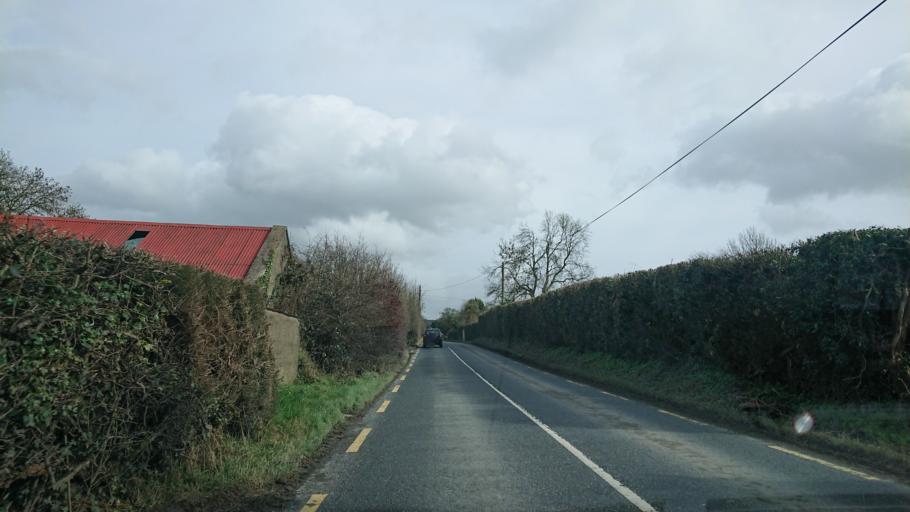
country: IE
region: Leinster
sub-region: Kildare
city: Eadestown
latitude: 53.1959
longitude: -6.5672
